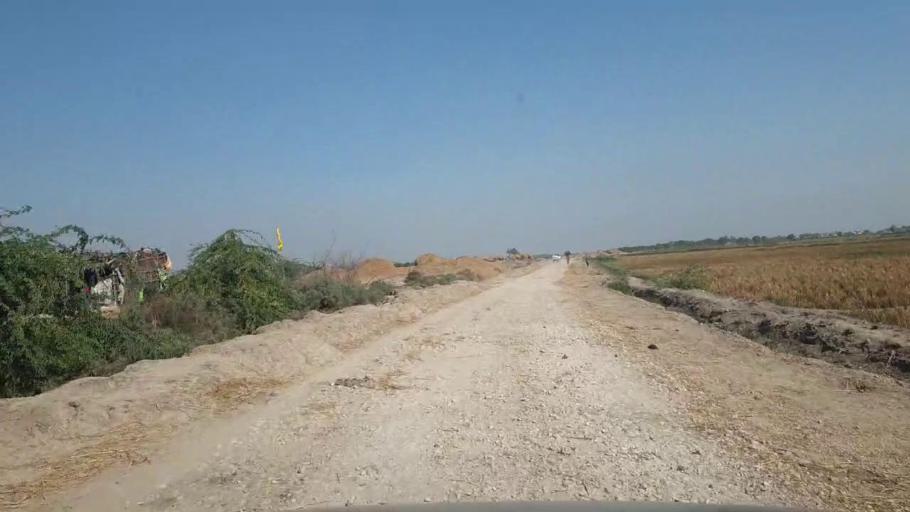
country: PK
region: Sindh
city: Talhar
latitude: 24.7819
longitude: 68.7855
